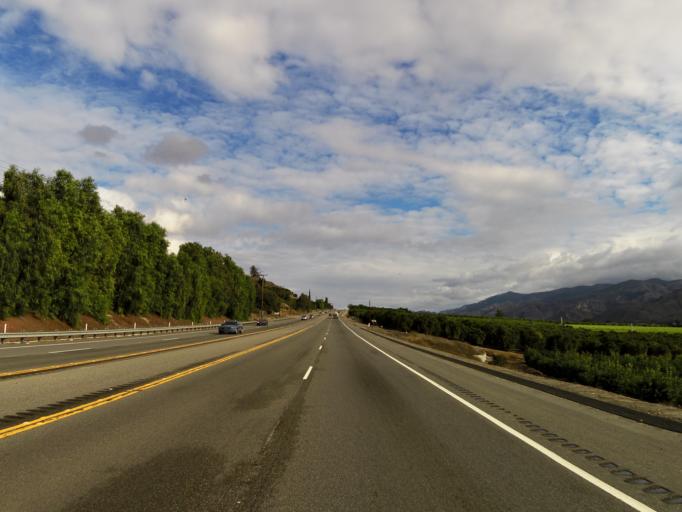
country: US
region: California
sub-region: Ventura County
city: Fillmore
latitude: 34.3955
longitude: -118.8719
